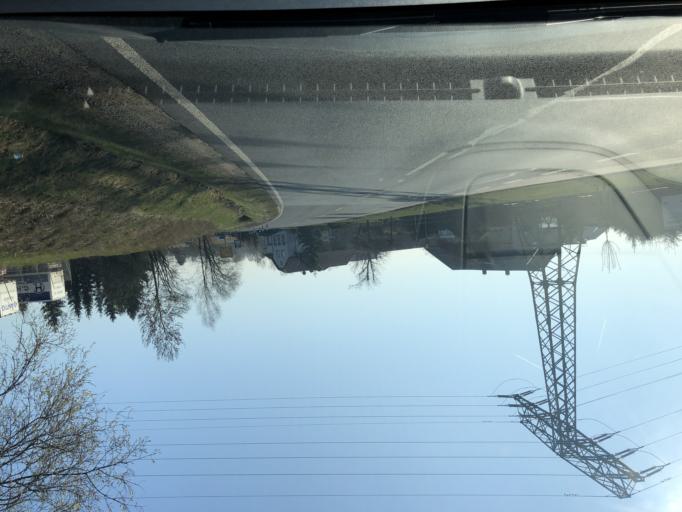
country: DE
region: Saxony
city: Ohorn
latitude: 51.1614
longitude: 14.0542
